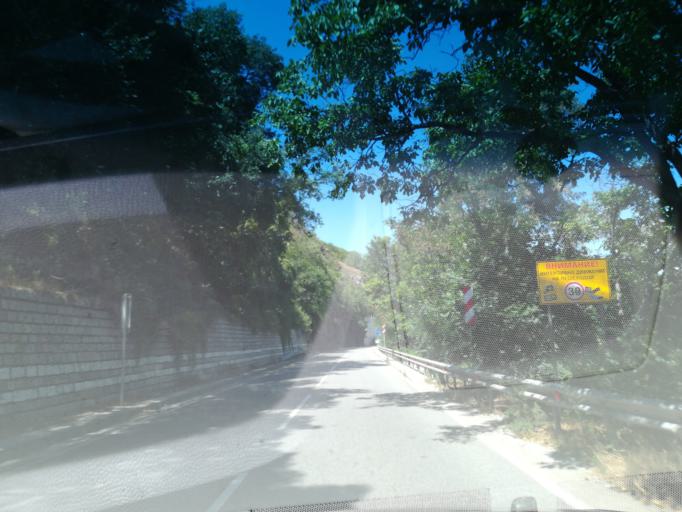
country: BG
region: Plovdiv
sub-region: Obshtina Asenovgrad
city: Asenovgrad
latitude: 41.9984
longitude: 24.8726
